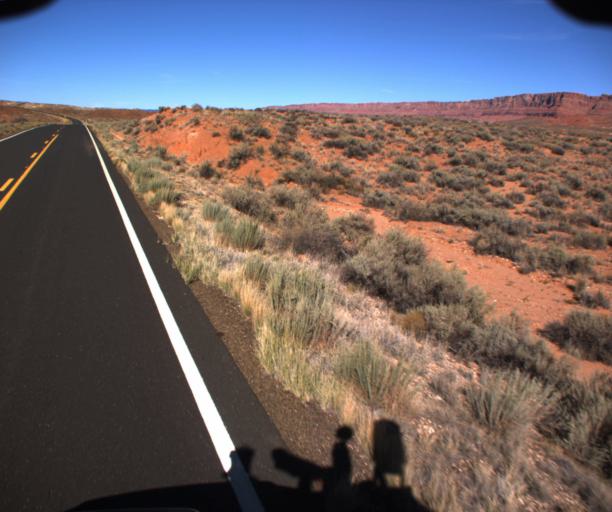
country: US
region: Arizona
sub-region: Coconino County
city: Page
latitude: 36.6882
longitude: -111.8722
